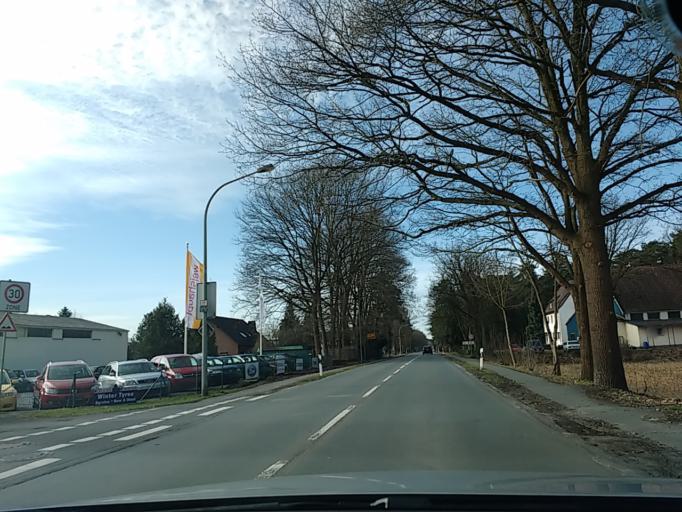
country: DE
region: North Rhine-Westphalia
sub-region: Regierungsbezirk Detmold
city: Paderborn
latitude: 51.7734
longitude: 8.7103
